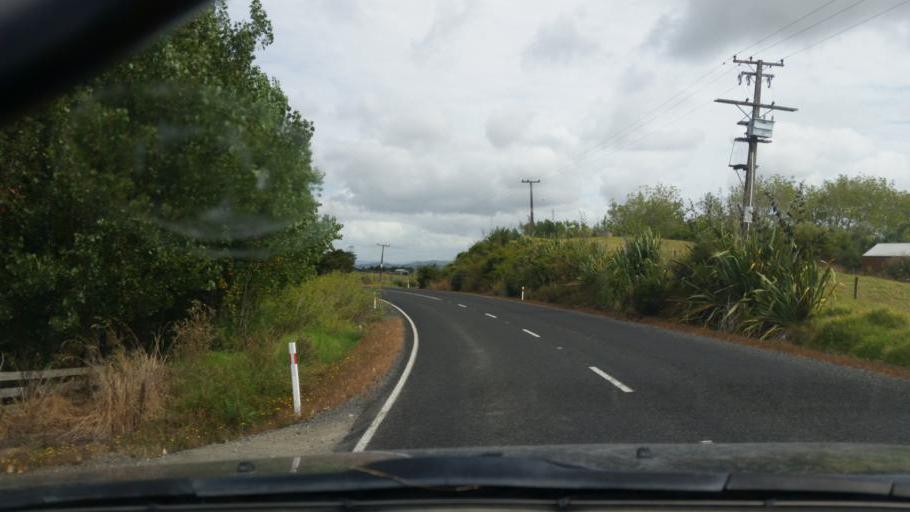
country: NZ
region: Northland
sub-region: Kaipara District
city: Dargaville
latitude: -35.9520
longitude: 173.9210
